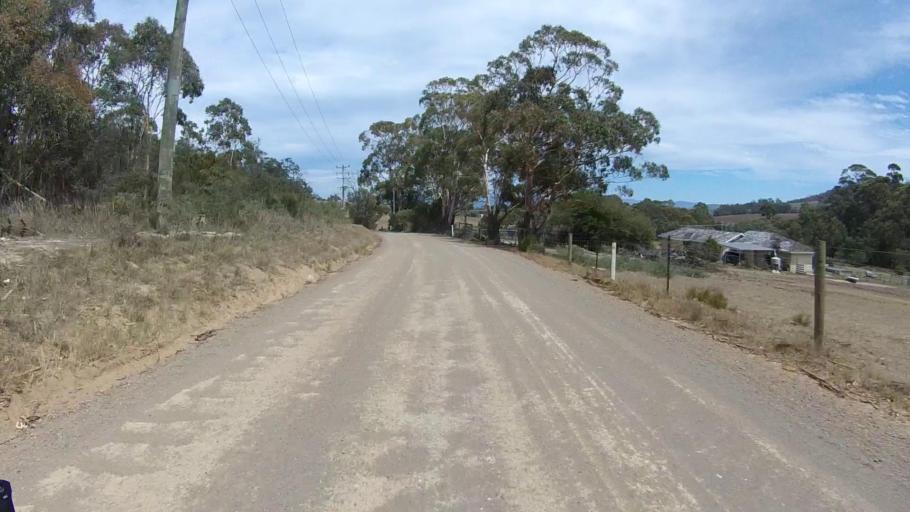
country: AU
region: Tasmania
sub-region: Sorell
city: Sorell
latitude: -42.8004
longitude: 147.6470
